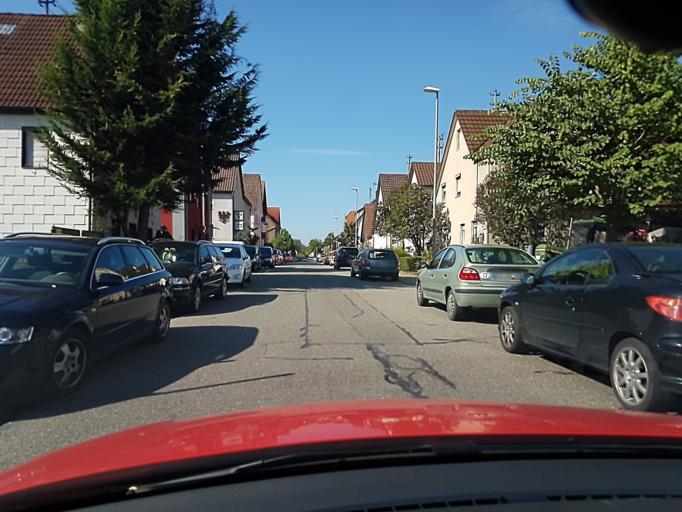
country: DE
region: Baden-Wuerttemberg
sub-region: Regierungsbezirk Stuttgart
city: Nordheim
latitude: 49.1067
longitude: 9.1321
